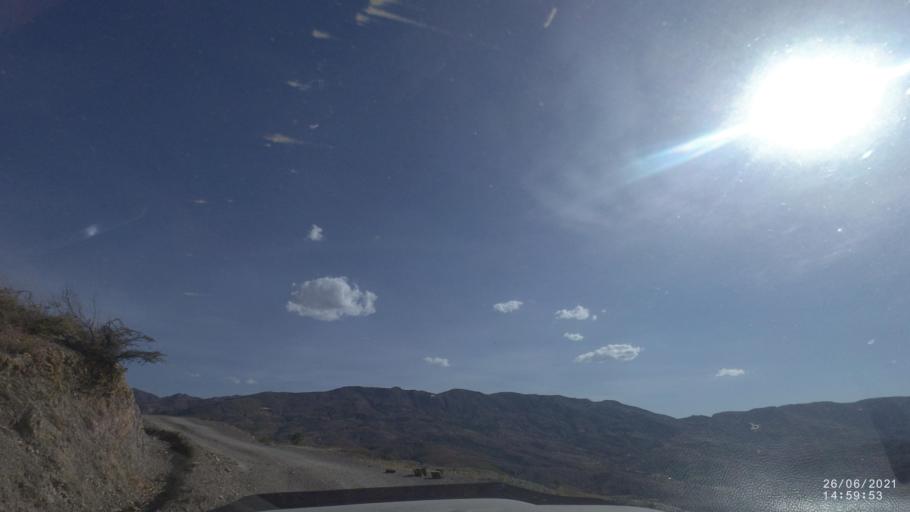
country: BO
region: Cochabamba
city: Mizque
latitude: -17.9486
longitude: -65.6202
